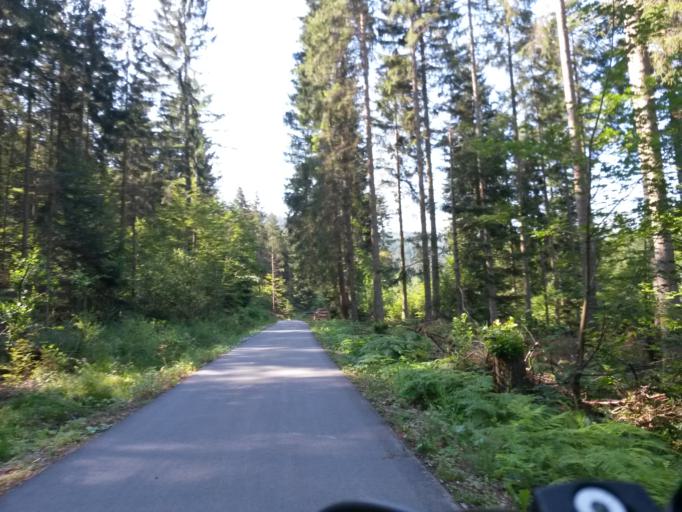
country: DE
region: Baden-Wuerttemberg
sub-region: Karlsruhe Region
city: Bad Wildbad
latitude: 48.7142
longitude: 8.5438
